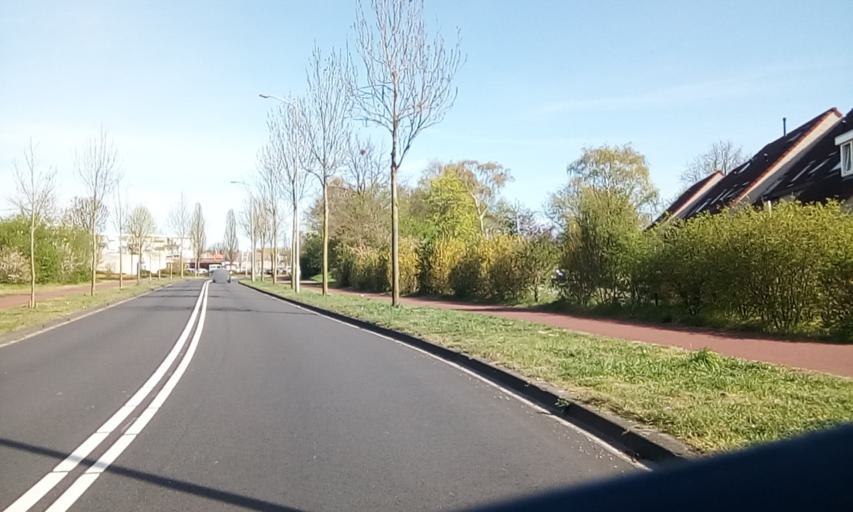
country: NL
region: Gelderland
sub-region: Gemeente Wijchen
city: Wijchen
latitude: 51.7995
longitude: 5.7212
